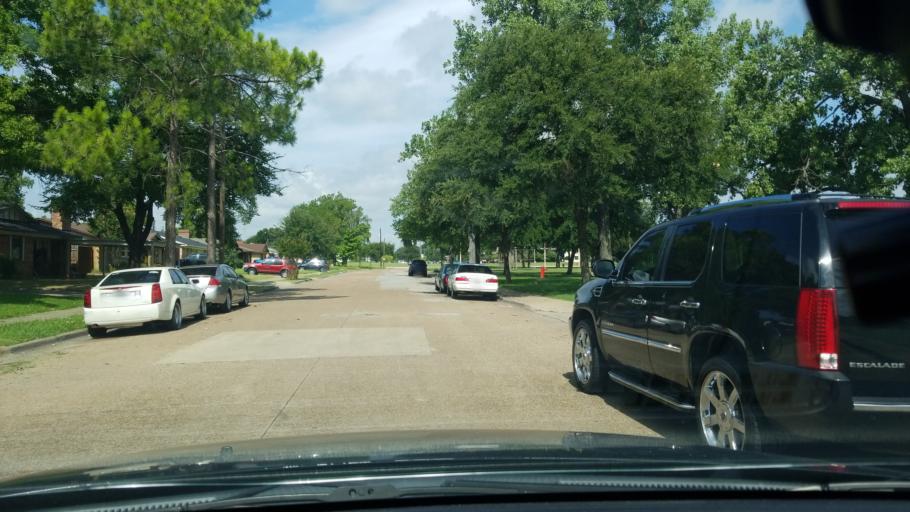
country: US
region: Texas
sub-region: Dallas County
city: Mesquite
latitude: 32.8181
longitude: -96.6546
